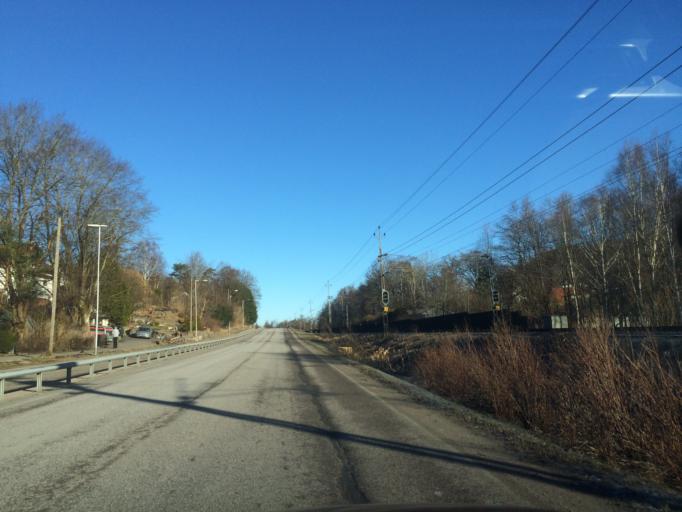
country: SE
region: Vaestra Goetaland
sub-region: Molndal
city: Lindome
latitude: 57.5802
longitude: 12.0760
